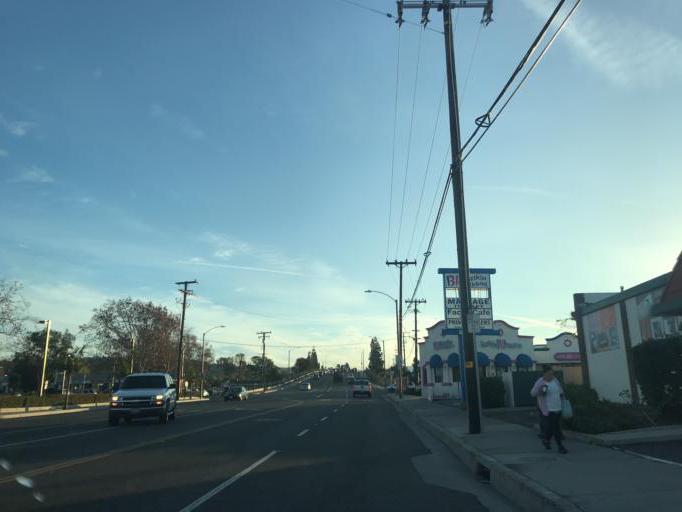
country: US
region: California
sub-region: Orange County
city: Villa Park
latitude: 33.8228
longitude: -117.8363
